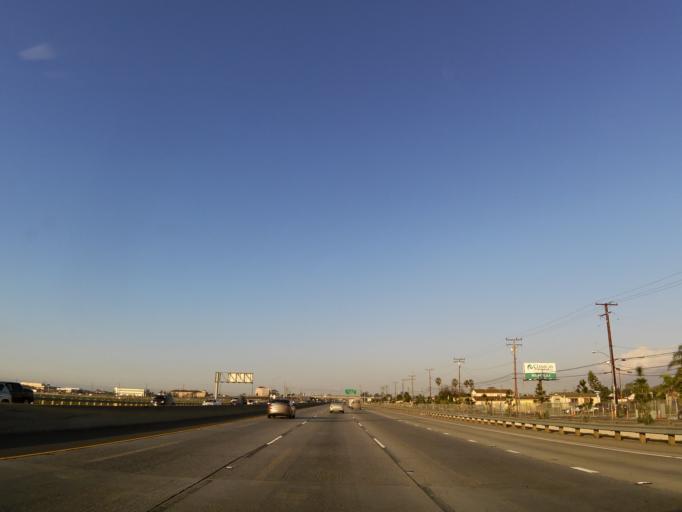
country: US
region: California
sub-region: Ventura County
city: El Rio
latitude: 34.2222
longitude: -119.1333
